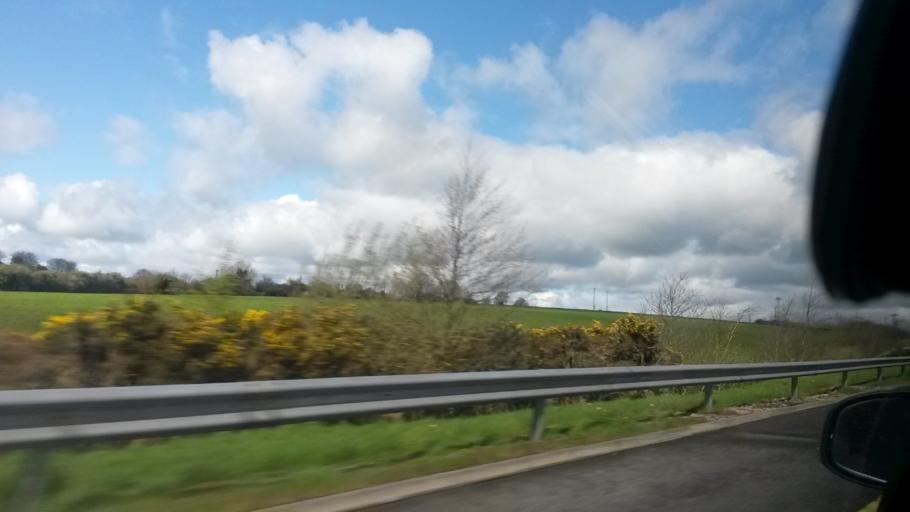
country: IE
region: Munster
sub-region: County Cork
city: Mitchelstown
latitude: 52.2134
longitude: -8.2779
